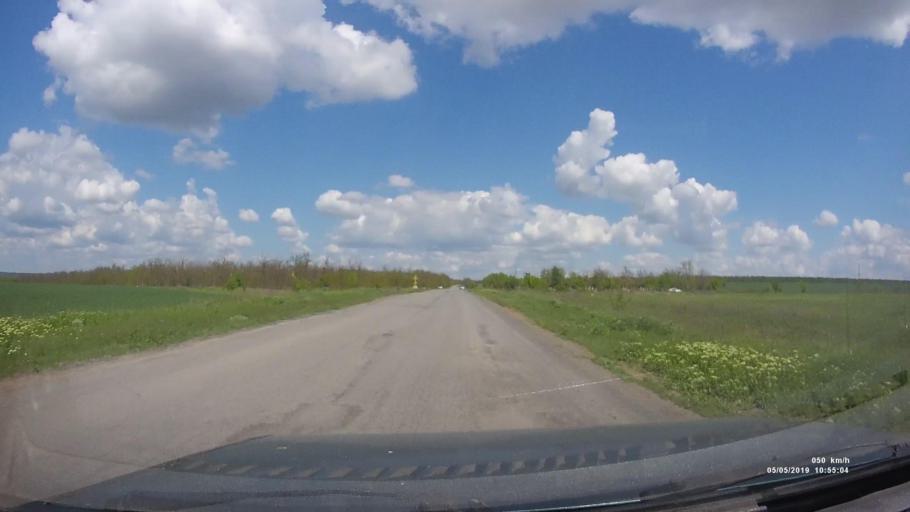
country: RU
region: Rostov
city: Ust'-Donetskiy
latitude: 47.6626
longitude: 40.8218
